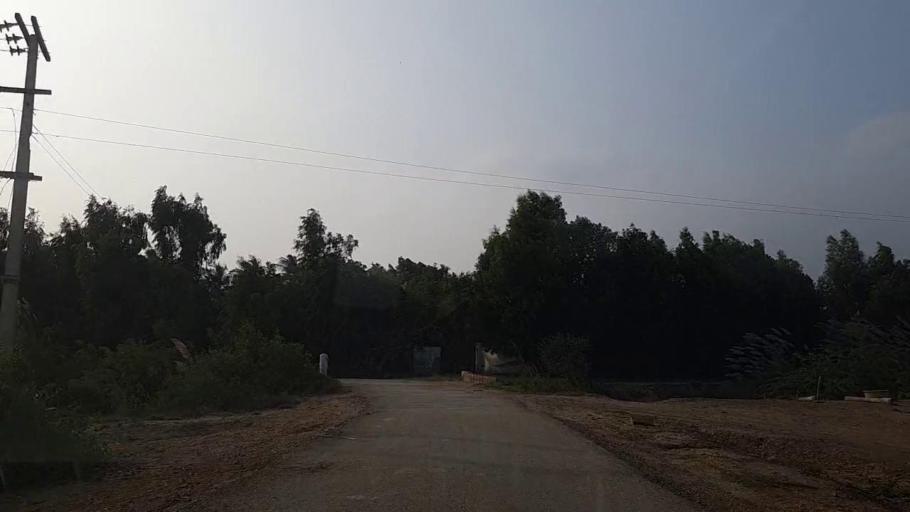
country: PK
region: Sindh
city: Mirpur Sakro
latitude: 24.6232
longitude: 67.5597
